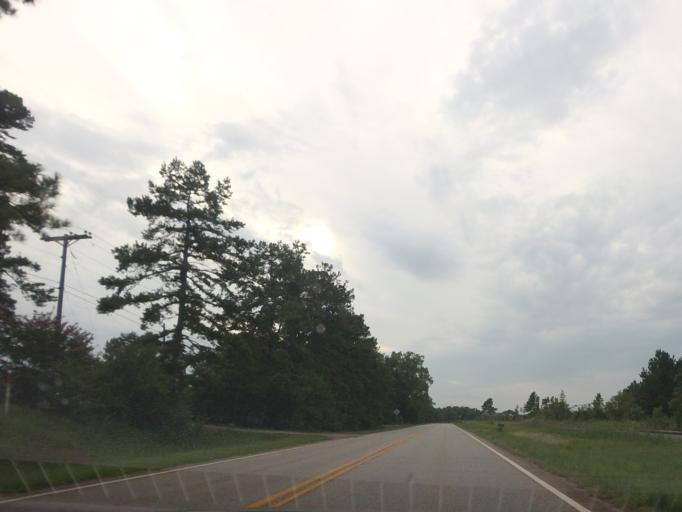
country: US
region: Georgia
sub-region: Twiggs County
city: Jeffersonville
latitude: 32.7177
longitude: -83.3968
